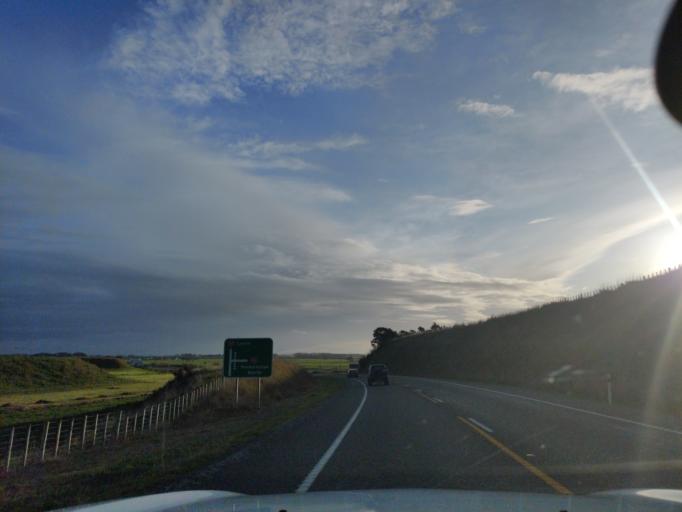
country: NZ
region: Manawatu-Wanganui
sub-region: Horowhenua District
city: Foxton
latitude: -40.5130
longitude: 175.4575
